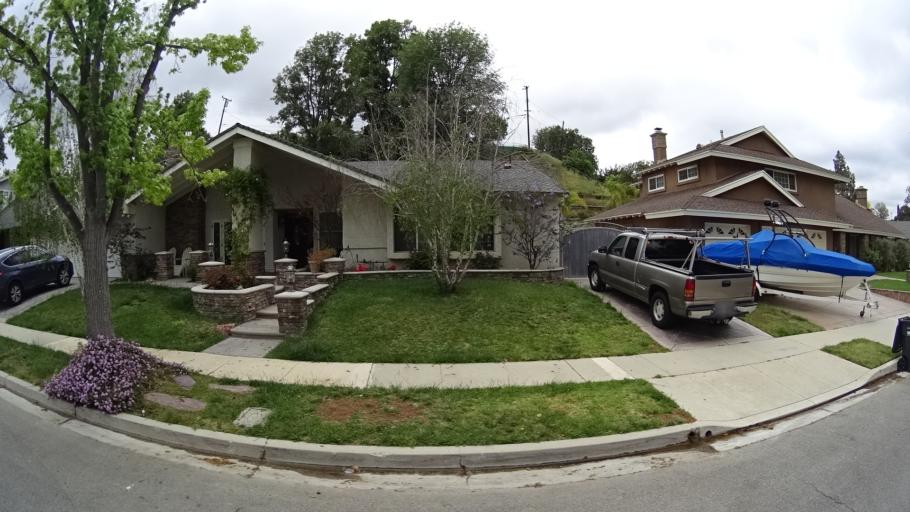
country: US
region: California
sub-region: Ventura County
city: Thousand Oaks
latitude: 34.2109
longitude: -118.8836
